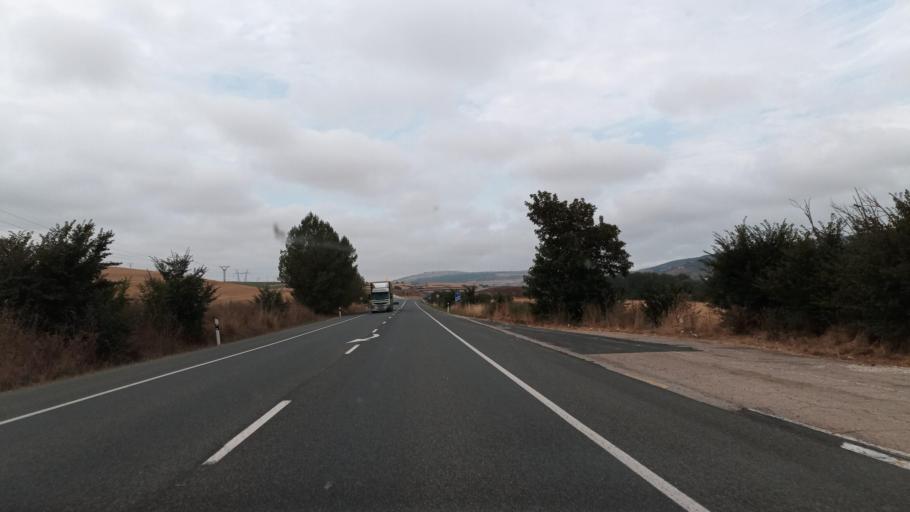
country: ES
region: Castille and Leon
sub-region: Provincia de Burgos
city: Castil de Peones
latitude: 42.4813
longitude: -3.3906
